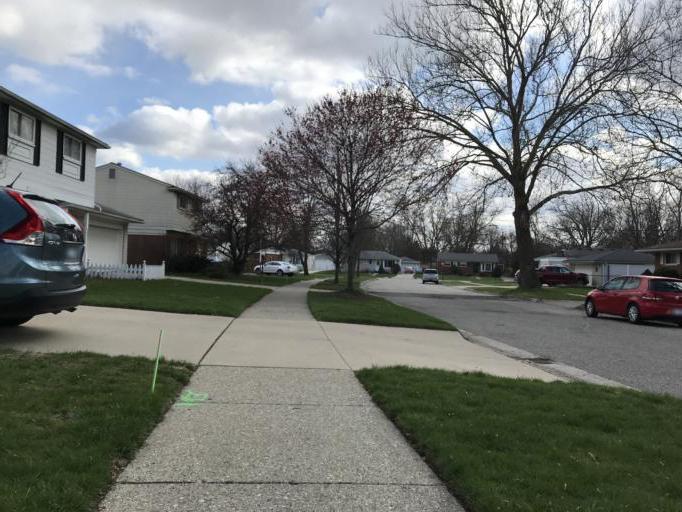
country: US
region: Michigan
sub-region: Oakland County
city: Farmington
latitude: 42.4600
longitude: -83.3437
